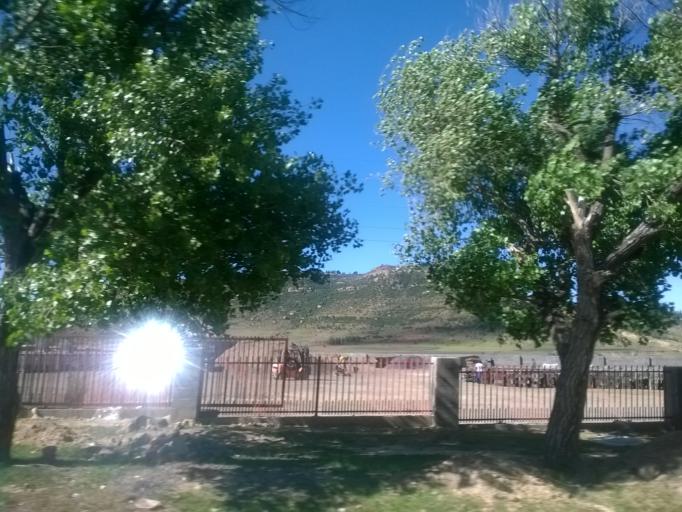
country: LS
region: Maseru
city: Maseru
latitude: -29.2679
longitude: 27.5844
